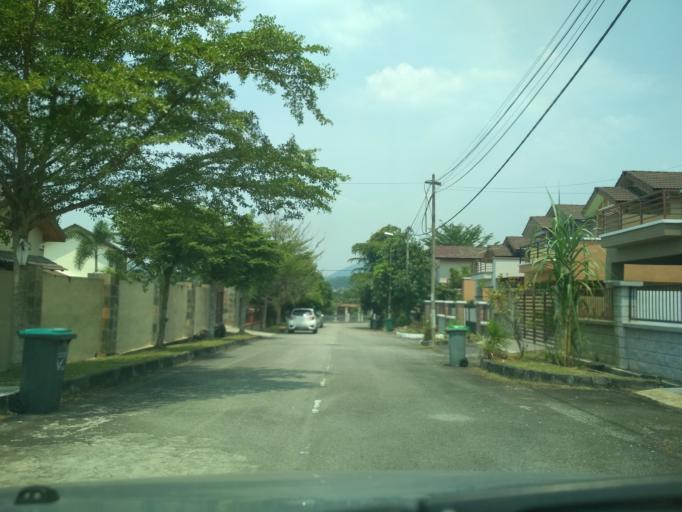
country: MY
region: Kedah
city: Kulim
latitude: 5.3593
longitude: 100.5363
